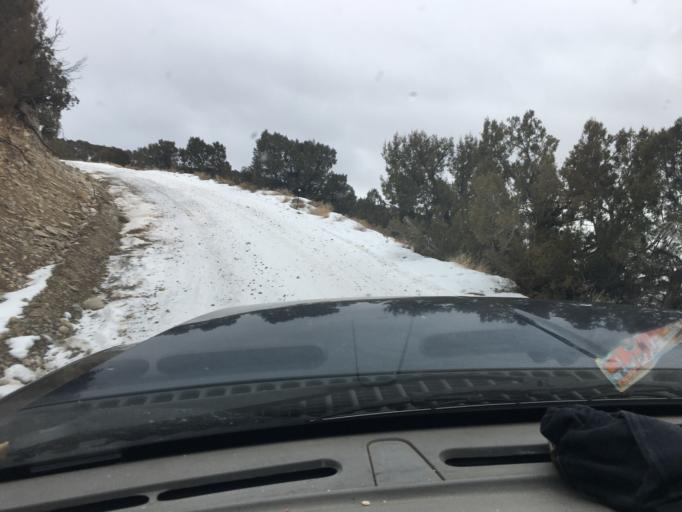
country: US
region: Colorado
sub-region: Garfield County
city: Parachute
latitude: 39.3470
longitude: -108.1728
